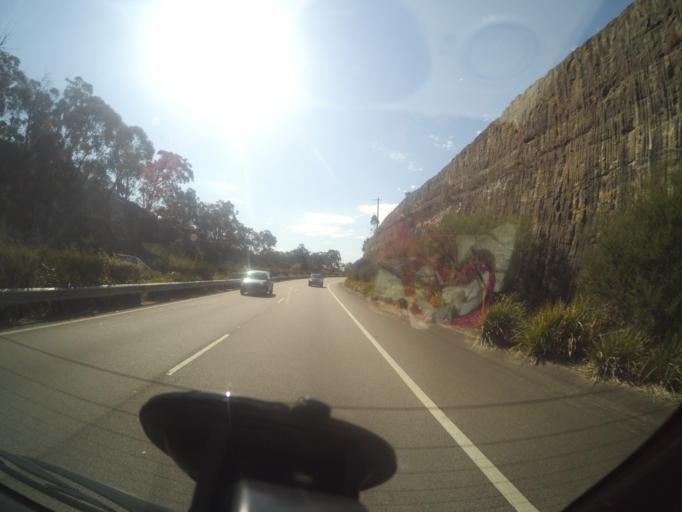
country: AU
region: New South Wales
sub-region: Blue Mountains Municipality
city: Hazelbrook
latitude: -33.7287
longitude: 150.4900
